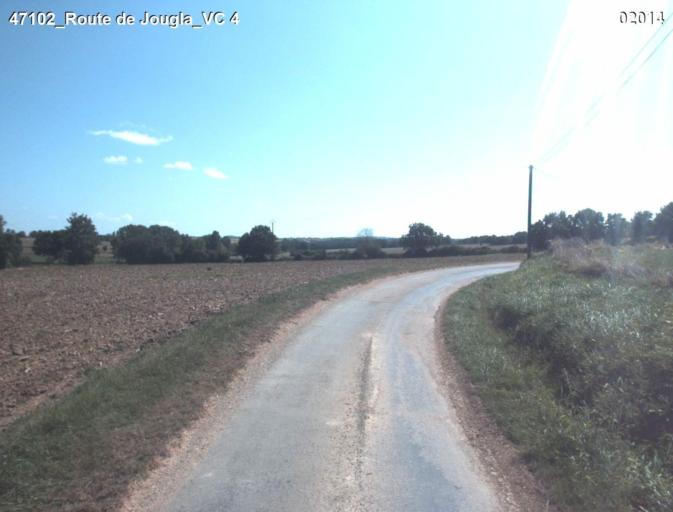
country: FR
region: Aquitaine
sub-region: Departement du Lot-et-Garonne
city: Nerac
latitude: 44.0586
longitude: 0.4320
